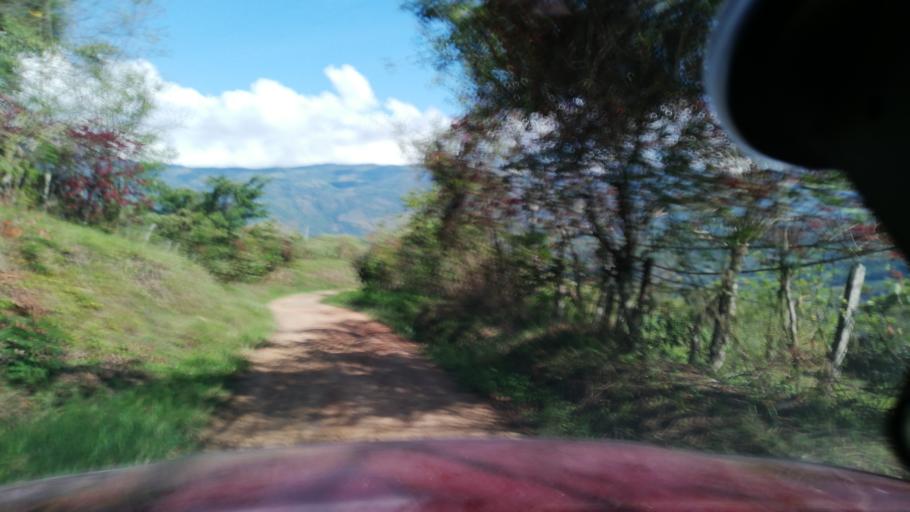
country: CO
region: Cundinamarca
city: Quipile
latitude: 4.7418
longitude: -74.6139
